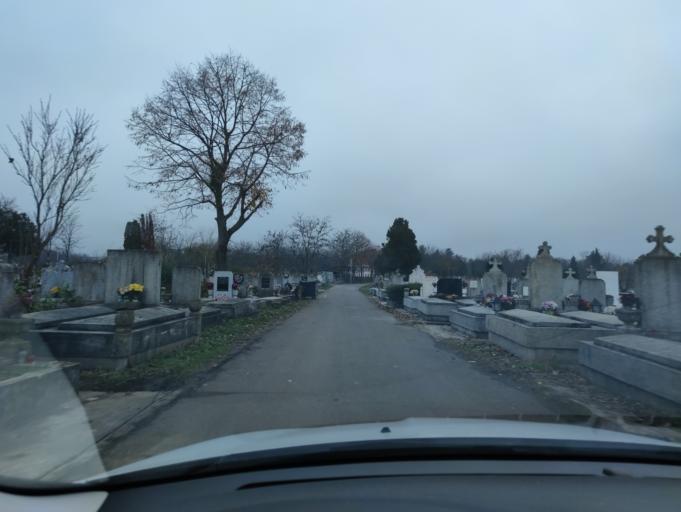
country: RO
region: Bihor
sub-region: Comuna Biharea
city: Oradea
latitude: 47.0390
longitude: 21.9255
